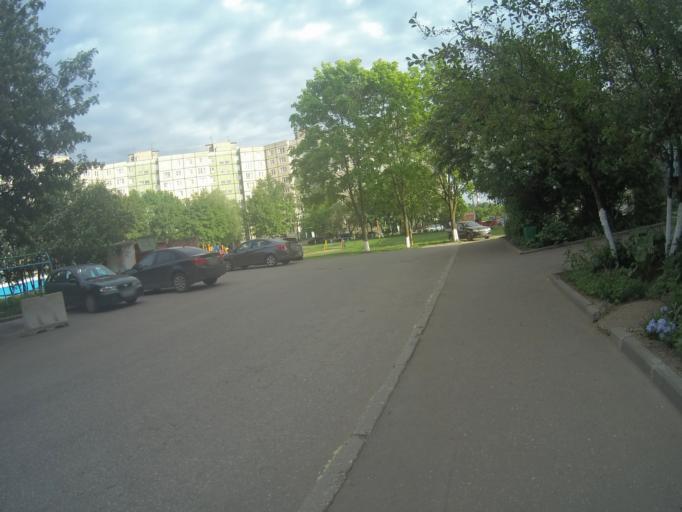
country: RU
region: Vladimir
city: Kommunar
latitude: 56.1616
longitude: 40.4546
